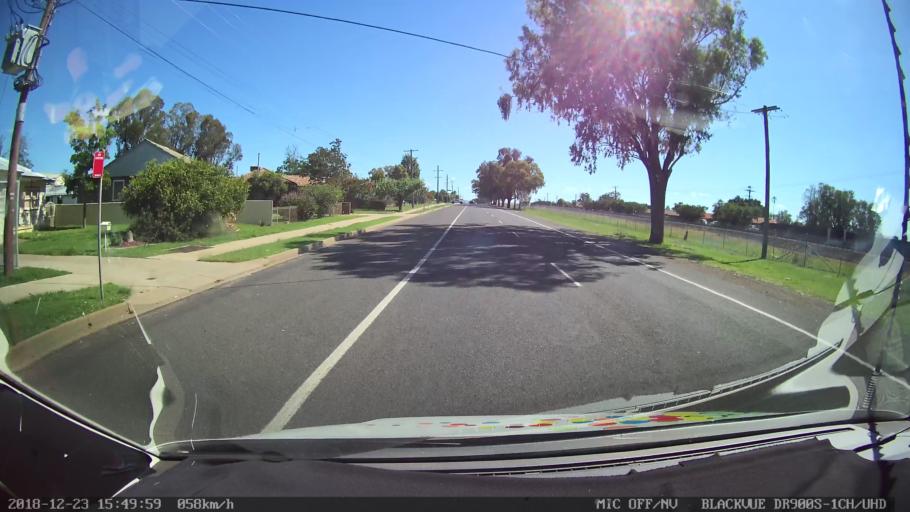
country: AU
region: New South Wales
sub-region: Tamworth Municipality
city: South Tamworth
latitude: -31.1029
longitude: 150.9032
